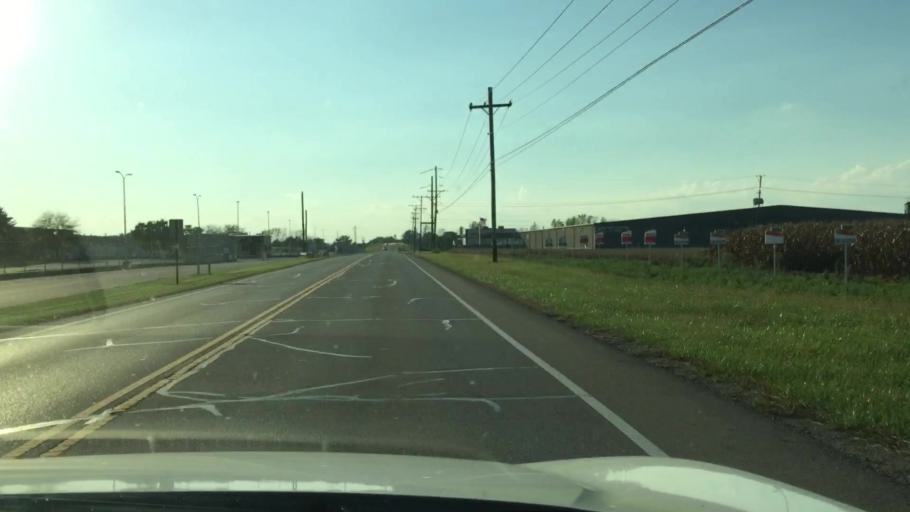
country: US
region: Ohio
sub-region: Champaign County
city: Urbana
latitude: 40.0908
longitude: -83.7702
